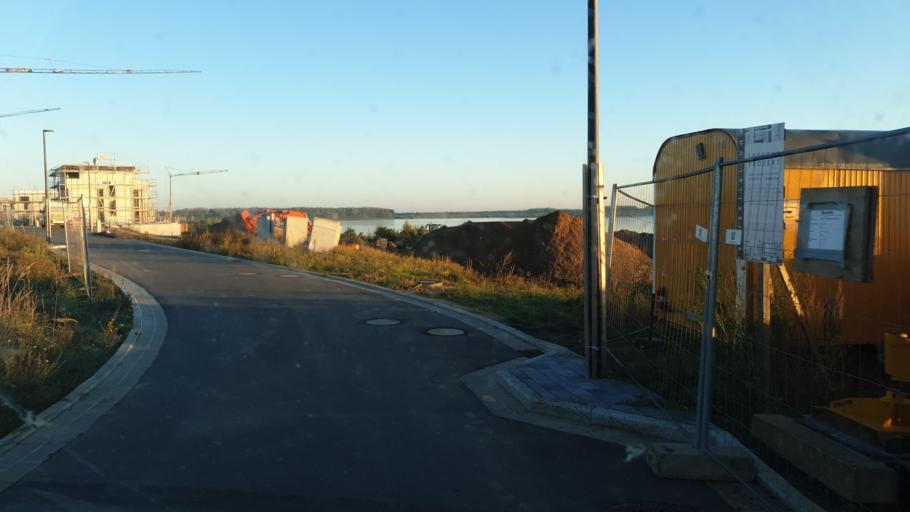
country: DE
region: Saxony
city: Zwenkau
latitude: 51.2268
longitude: 12.3399
